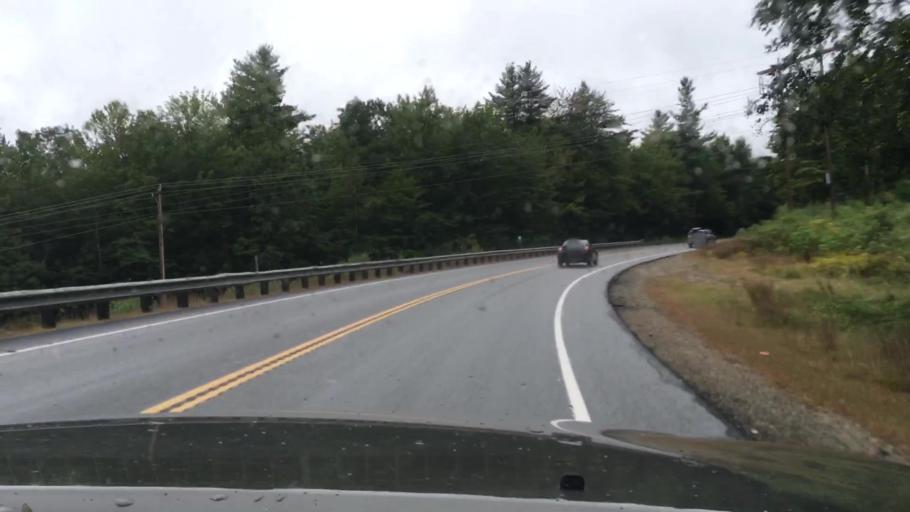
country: US
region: New Hampshire
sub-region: Hillsborough County
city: Antrim
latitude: 43.0668
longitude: -72.0558
